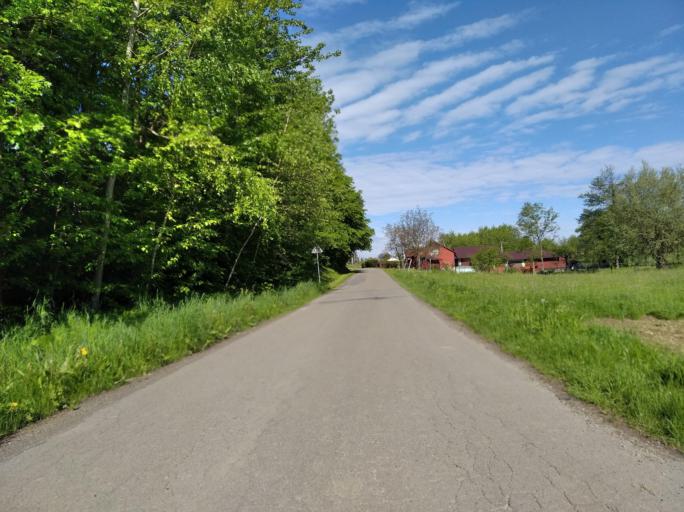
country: PL
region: Subcarpathian Voivodeship
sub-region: Powiat strzyzowski
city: Frysztak
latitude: 49.8460
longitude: 21.5391
